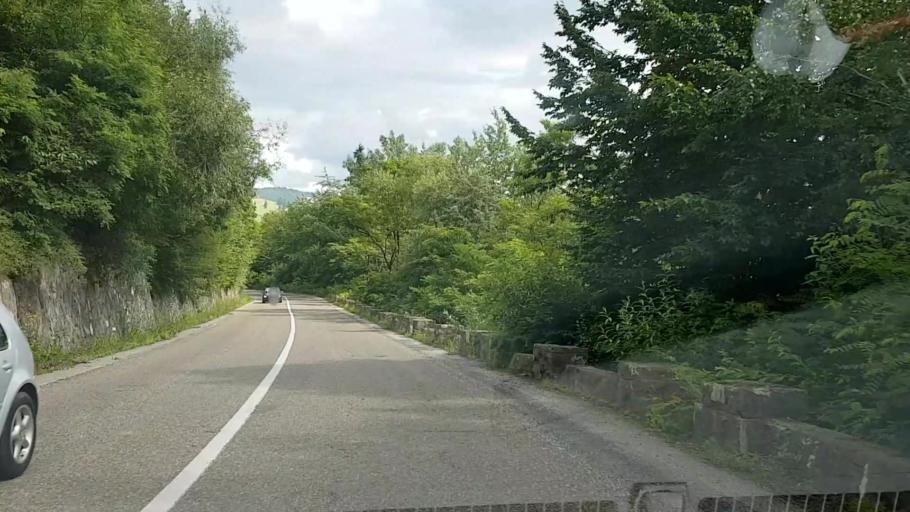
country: RO
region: Neamt
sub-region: Comuna Ceahlau
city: Ceahlau
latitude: 47.0556
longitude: 25.9713
